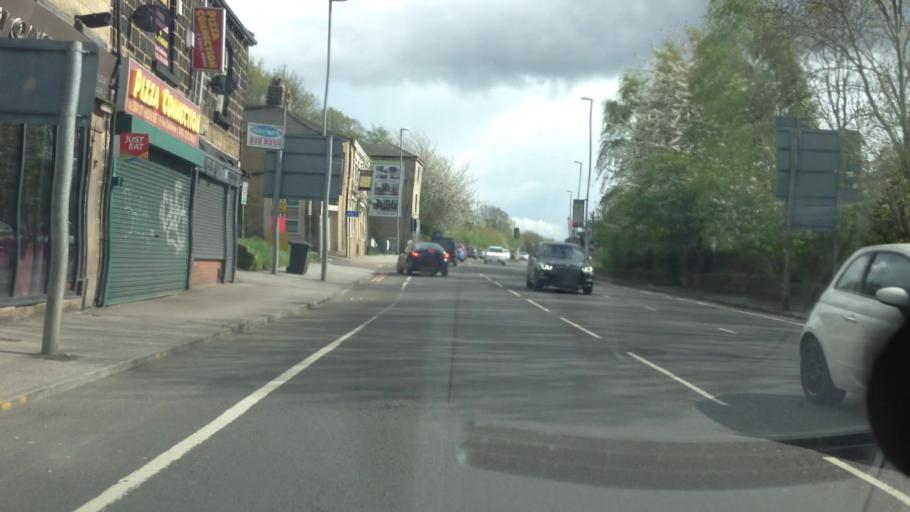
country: GB
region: England
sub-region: City and Borough of Leeds
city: Horsforth
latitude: 53.8150
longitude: -1.6013
